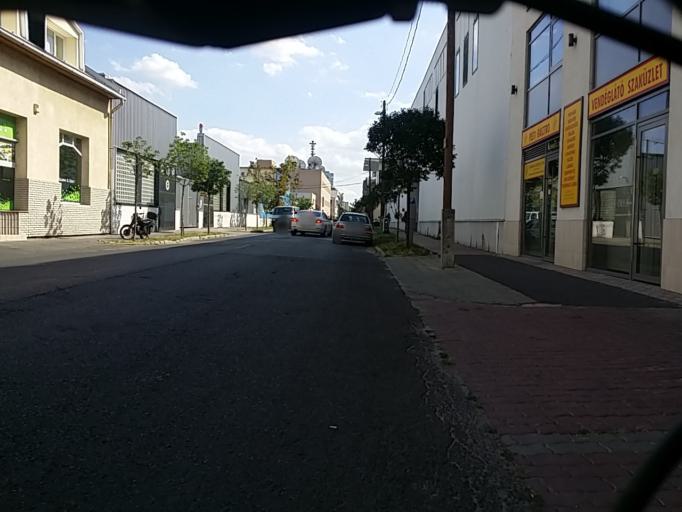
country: HU
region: Budapest
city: Budapest XIII. keruelet
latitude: 47.5387
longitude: 19.0714
